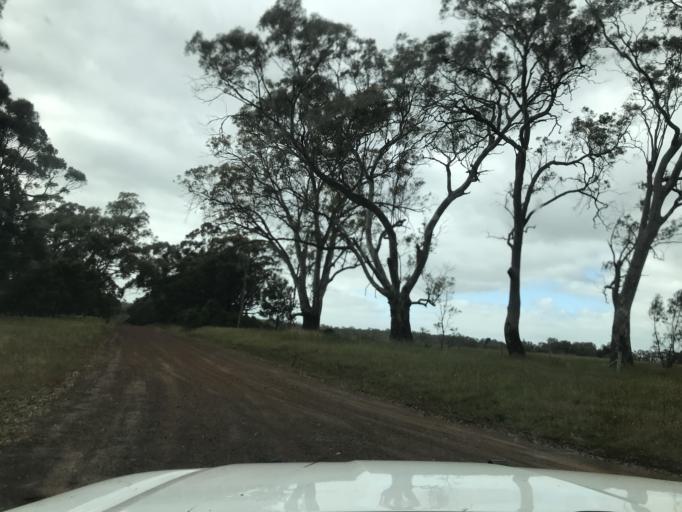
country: AU
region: South Australia
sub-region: Wattle Range
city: Penola
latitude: -37.3147
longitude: 141.4010
